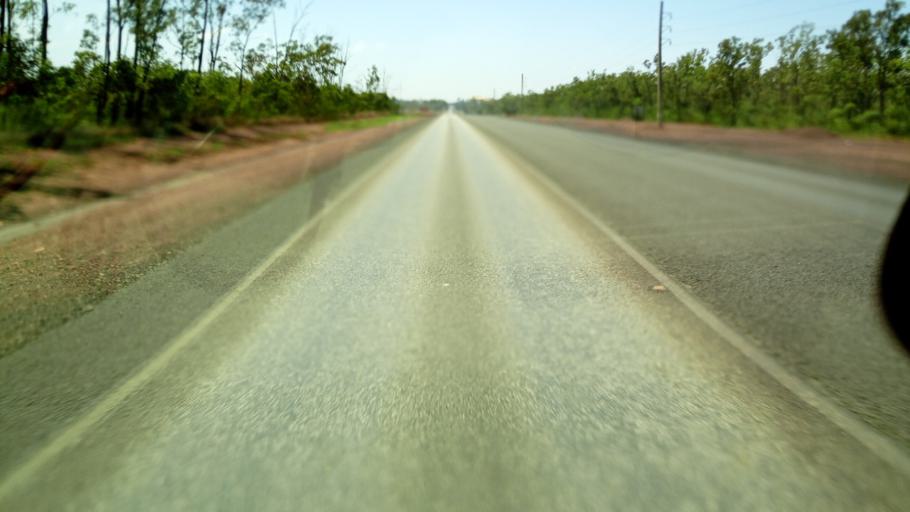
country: AU
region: Northern Territory
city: Alyangula
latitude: -13.9651
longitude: 136.4428
